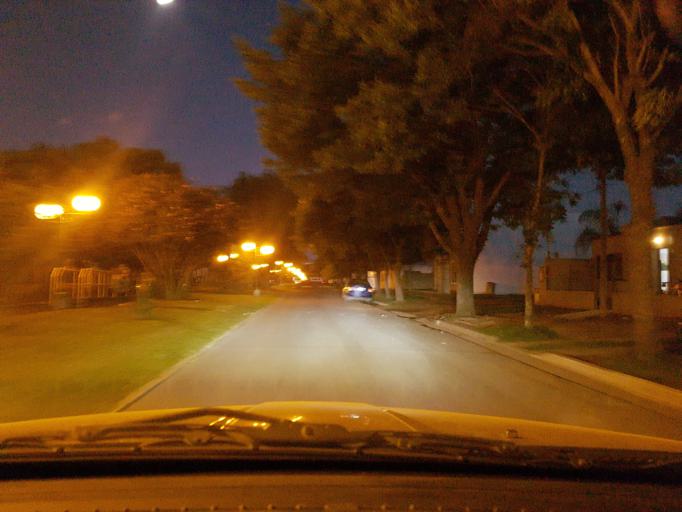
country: AR
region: Cordoba
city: Las Perdices
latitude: -32.7577
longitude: -63.7835
